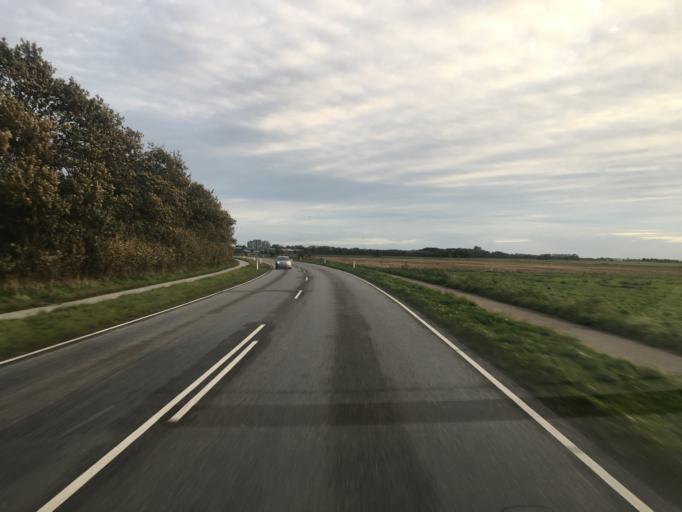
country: DK
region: South Denmark
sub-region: Tonder Kommune
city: Tonder
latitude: 54.9430
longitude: 8.8434
